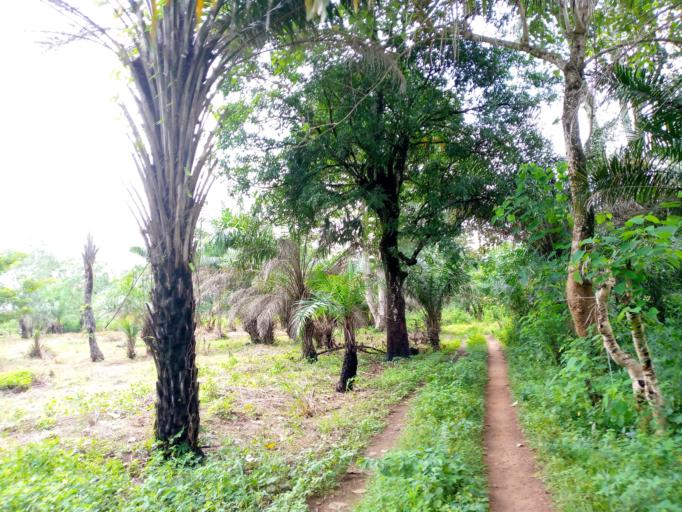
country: SL
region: Northern Province
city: Magburaka
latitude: 8.7262
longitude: -11.9322
